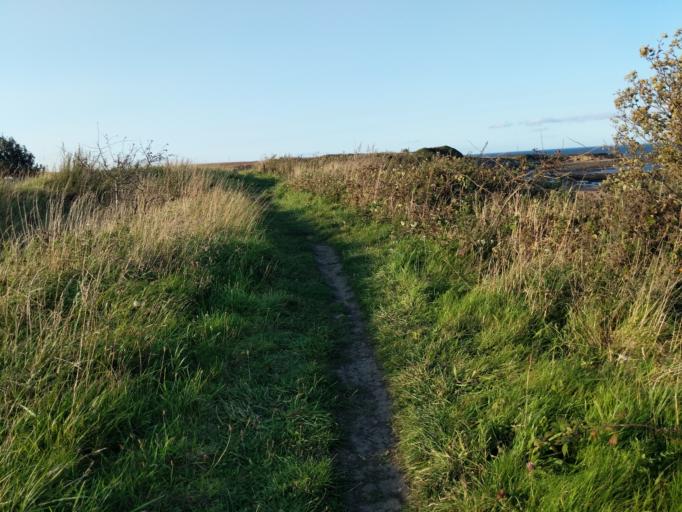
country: GB
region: England
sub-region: Northumberland
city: Lynemouth
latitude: 55.2224
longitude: -1.5299
